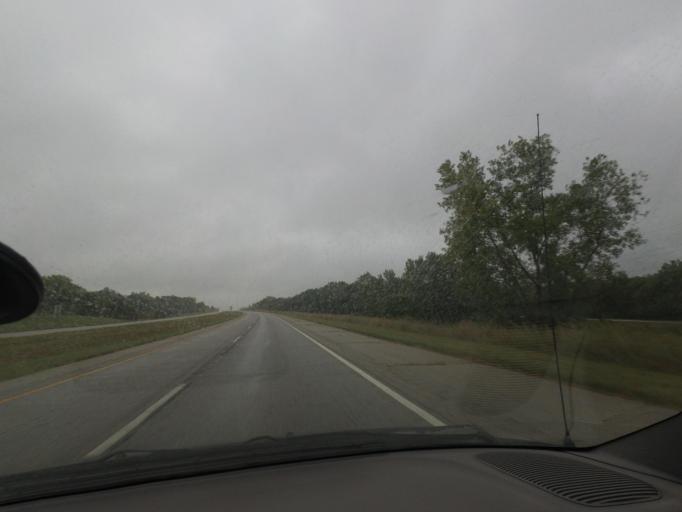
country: US
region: Illinois
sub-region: Pike County
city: Barry
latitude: 39.7089
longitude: -91.0552
